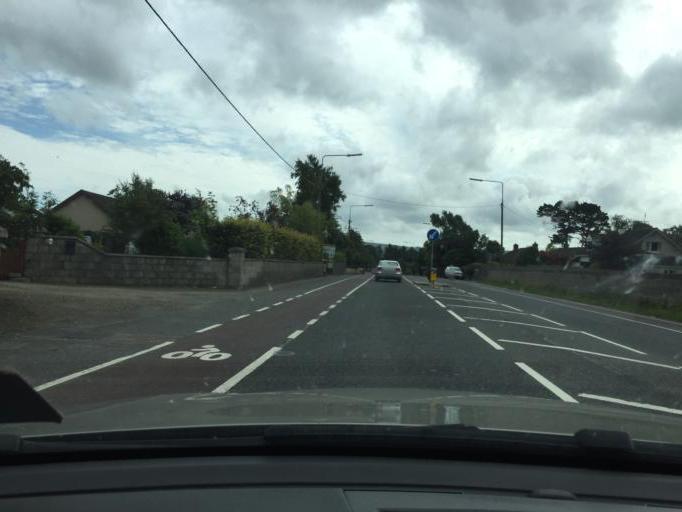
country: IE
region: Munster
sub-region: Waterford
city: Dungarvan
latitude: 52.1045
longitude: -7.6045
